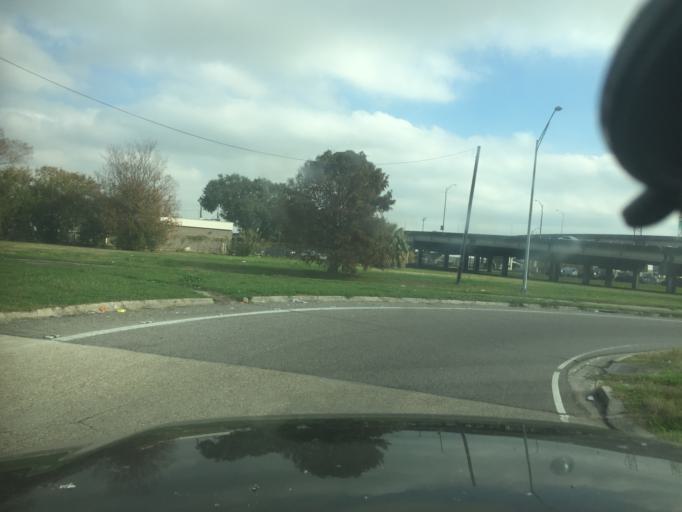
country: US
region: Louisiana
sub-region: Saint Bernard Parish
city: Arabi
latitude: 30.0033
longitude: -90.0370
